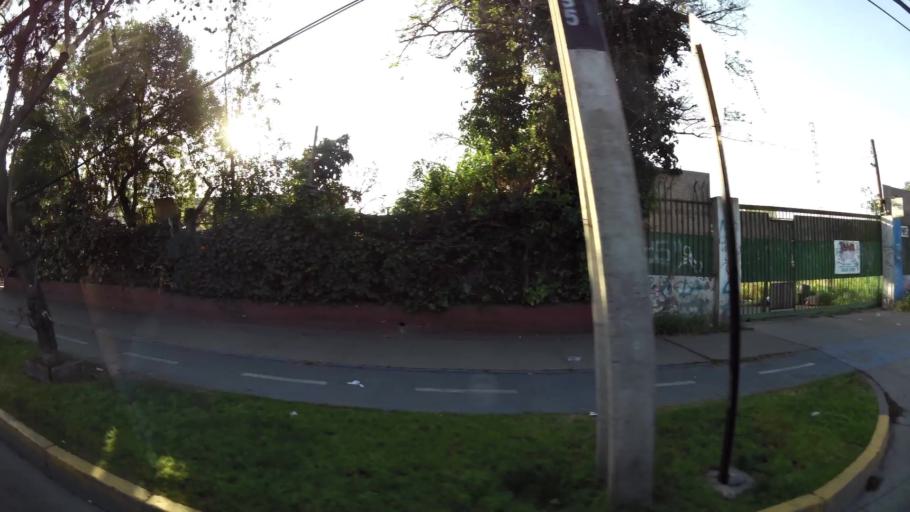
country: CL
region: Santiago Metropolitan
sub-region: Provincia de Santiago
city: Santiago
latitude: -33.3758
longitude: -70.6374
